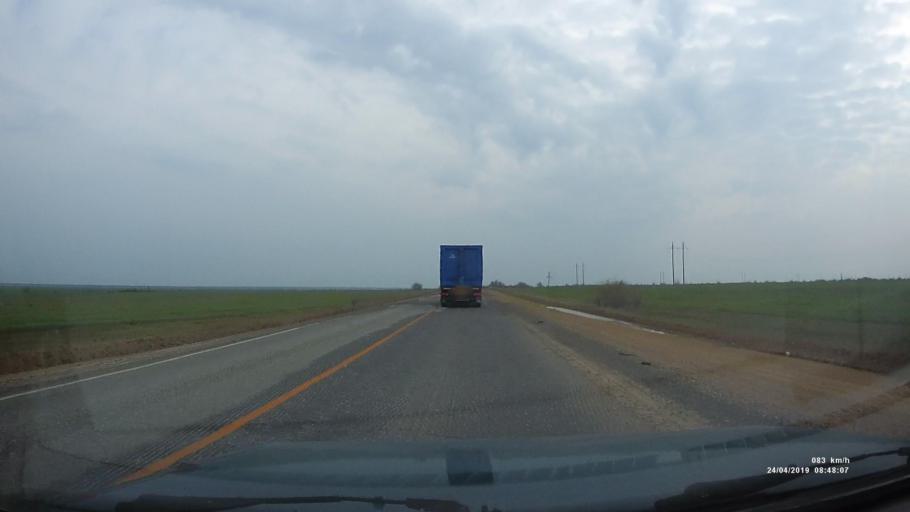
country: RU
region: Kalmykiya
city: Arshan'
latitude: 46.2492
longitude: 44.1041
